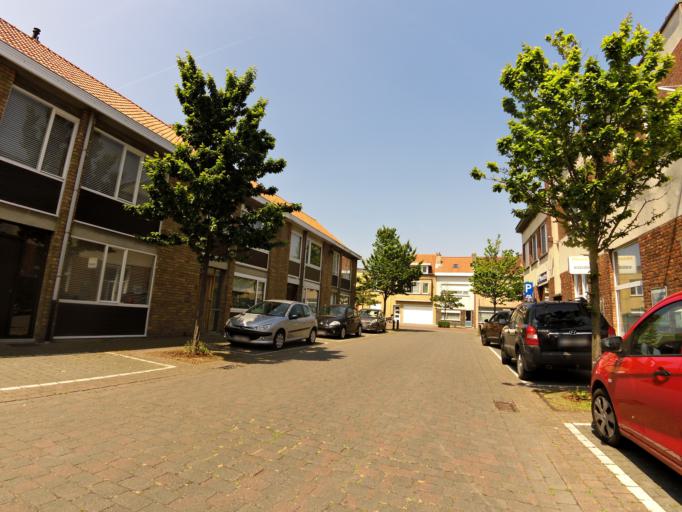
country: BE
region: Flanders
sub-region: Provincie West-Vlaanderen
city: Ostend
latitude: 51.2171
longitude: 2.9008
